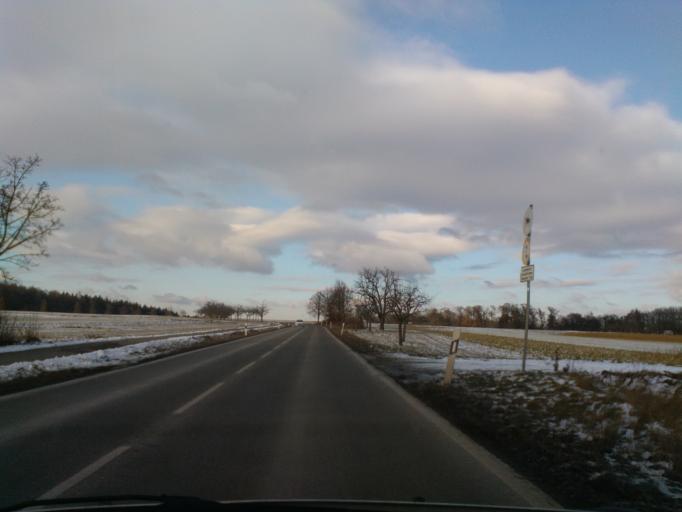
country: DE
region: Baden-Wuerttemberg
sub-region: Regierungsbezirk Stuttgart
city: Wolfschlugen
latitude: 48.6614
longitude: 9.2865
